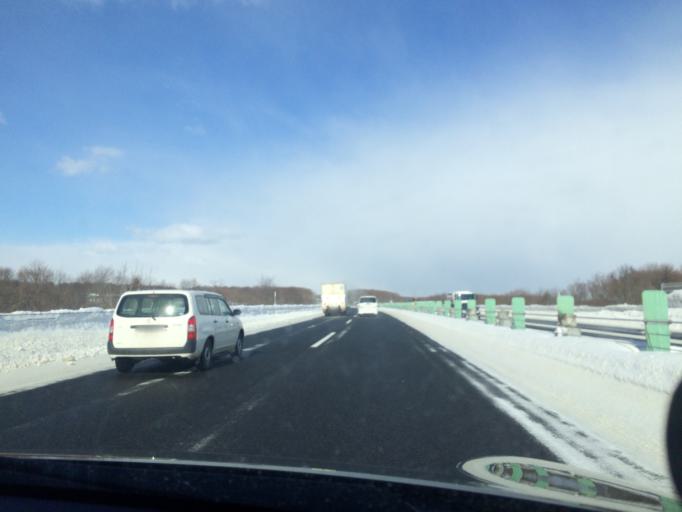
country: JP
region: Hokkaido
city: Kitahiroshima
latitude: 42.9118
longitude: 141.5495
